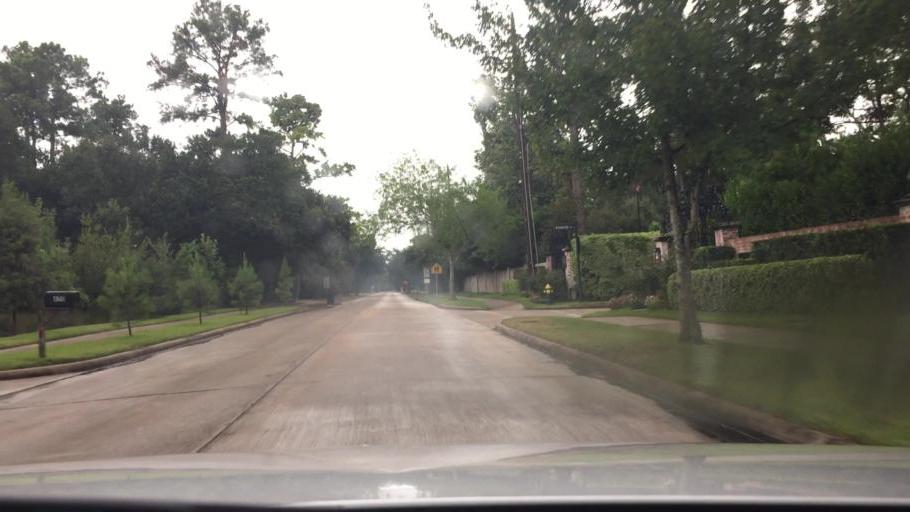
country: US
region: Texas
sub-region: Harris County
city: Hedwig Village
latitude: 29.7716
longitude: -95.5176
